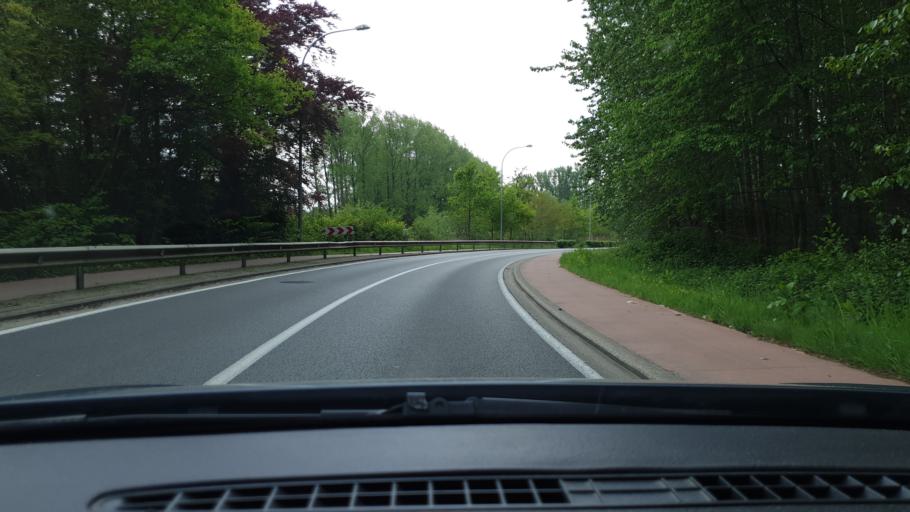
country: BE
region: Flanders
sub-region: Provincie Antwerpen
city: Balen
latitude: 51.1495
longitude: 5.1518
